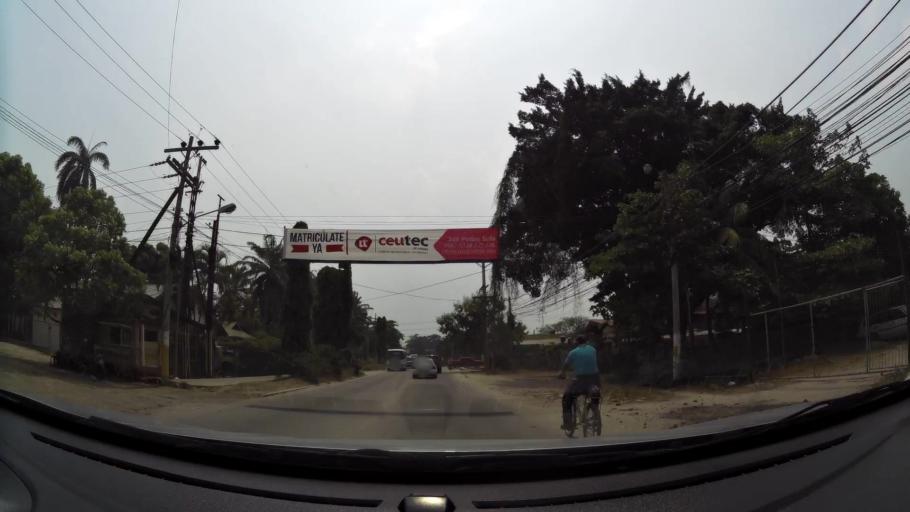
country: HN
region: Cortes
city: La Lima
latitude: 15.4367
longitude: -87.9225
